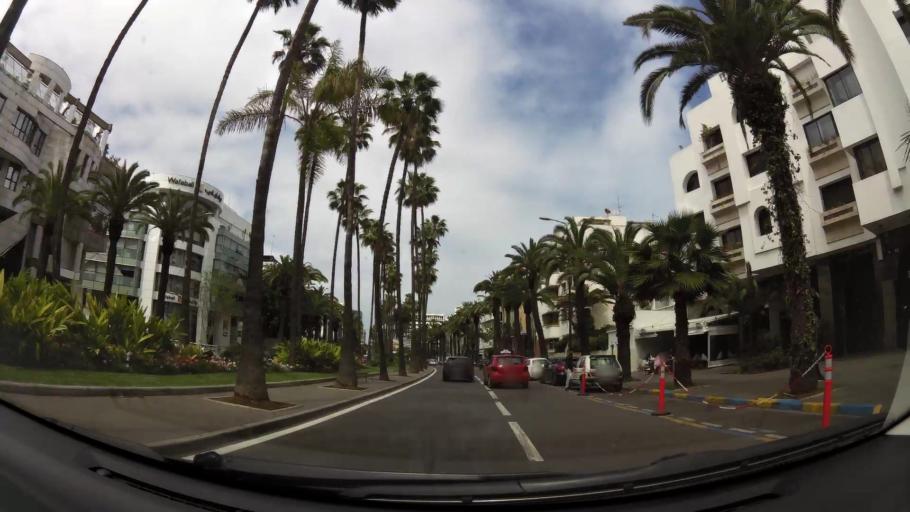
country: MA
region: Grand Casablanca
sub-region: Casablanca
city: Casablanca
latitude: 33.5916
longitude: -7.6273
